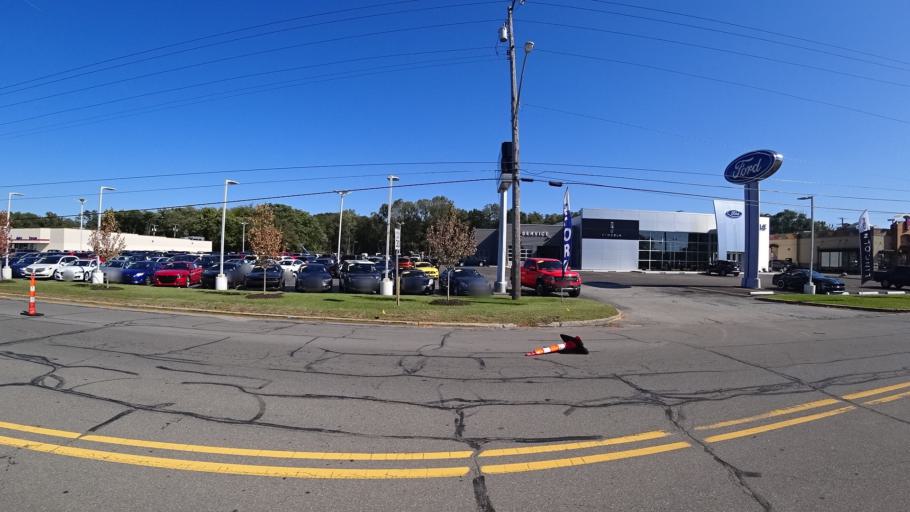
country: US
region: Indiana
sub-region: LaPorte County
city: Michigan City
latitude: 41.6835
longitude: -86.8939
